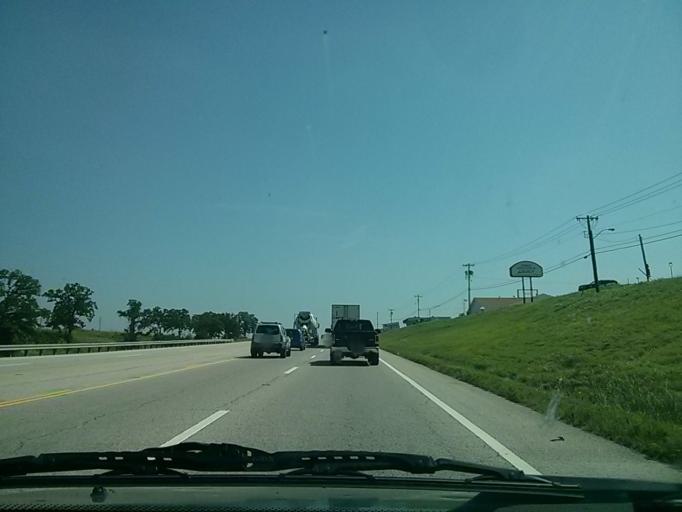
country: US
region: Oklahoma
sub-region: Creek County
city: Sapulpa
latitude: 36.0334
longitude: -96.0860
